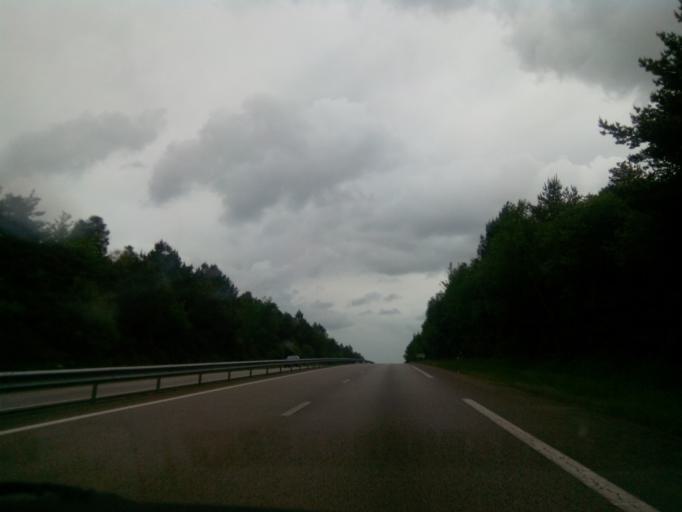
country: FR
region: Brittany
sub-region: Departement du Morbihan
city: Malestroit
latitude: 47.8126
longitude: -2.4412
